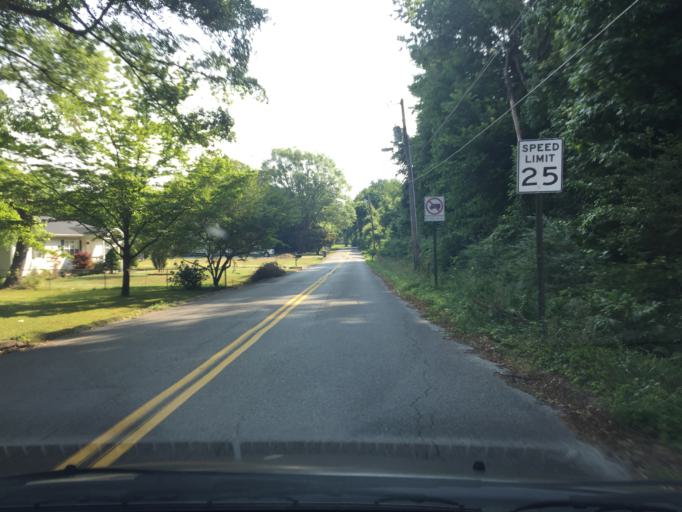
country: US
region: Tennessee
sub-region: Hamilton County
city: Falling Water
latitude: 35.1414
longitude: -85.2288
